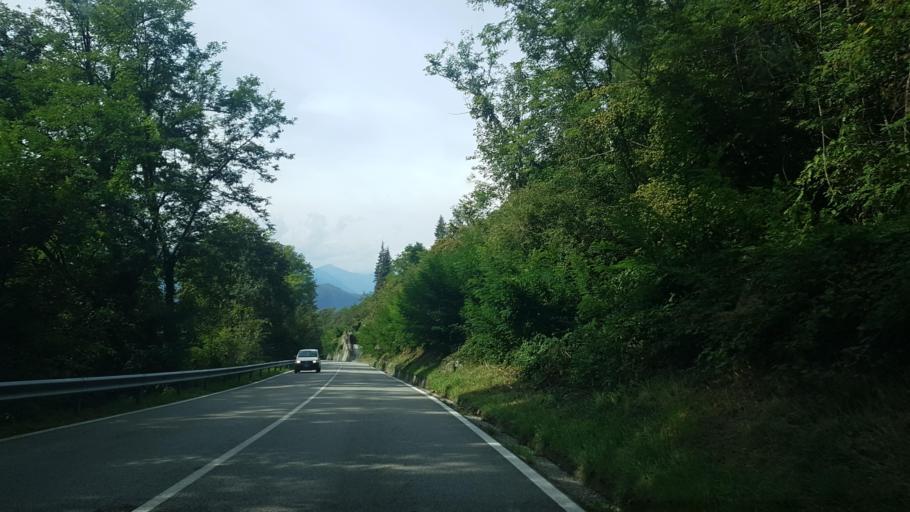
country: IT
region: Piedmont
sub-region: Provincia Verbano-Cusio-Ossola
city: Bee
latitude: 45.9621
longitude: 8.5745
